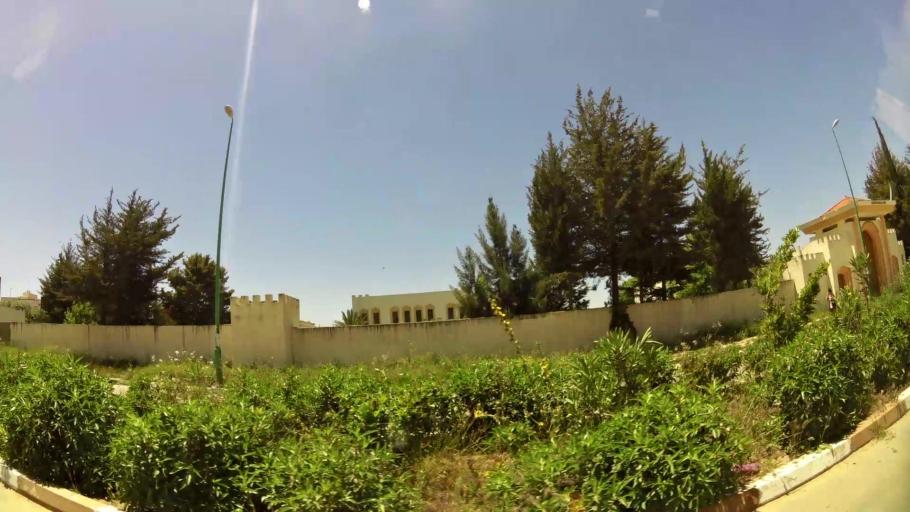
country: MA
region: Meknes-Tafilalet
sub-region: Meknes
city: Meknes
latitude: 33.8579
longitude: -5.5701
